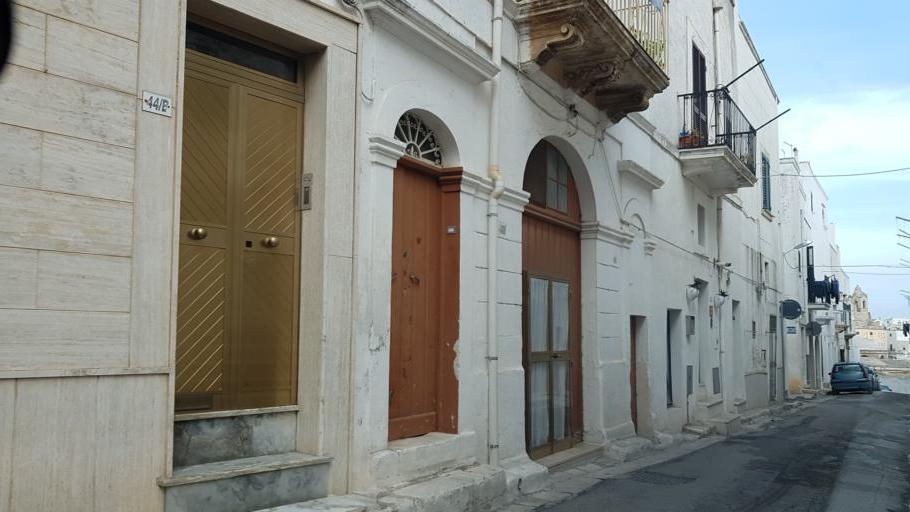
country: IT
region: Apulia
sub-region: Provincia di Brindisi
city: Ostuni
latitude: 40.7313
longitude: 17.5769
